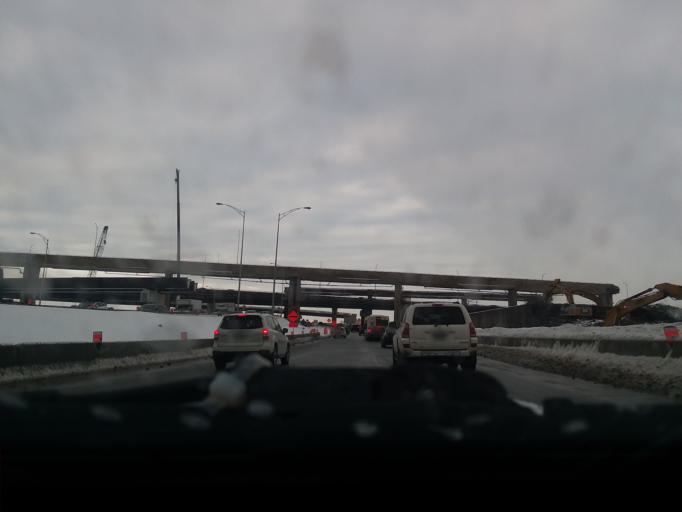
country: CA
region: Quebec
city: Saint-Raymond
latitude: 45.4666
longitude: -73.6022
